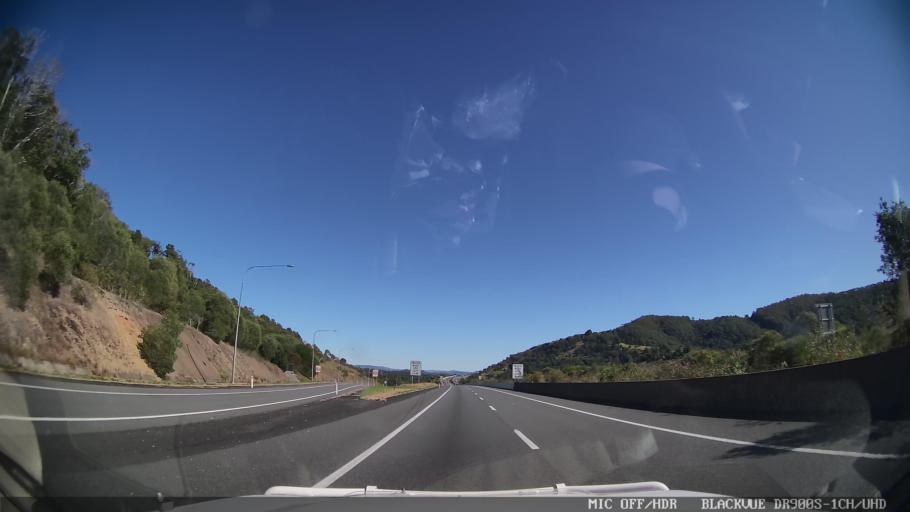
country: AU
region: Queensland
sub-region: Sunshine Coast
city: Black Mountain
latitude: -26.3889
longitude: 152.8015
